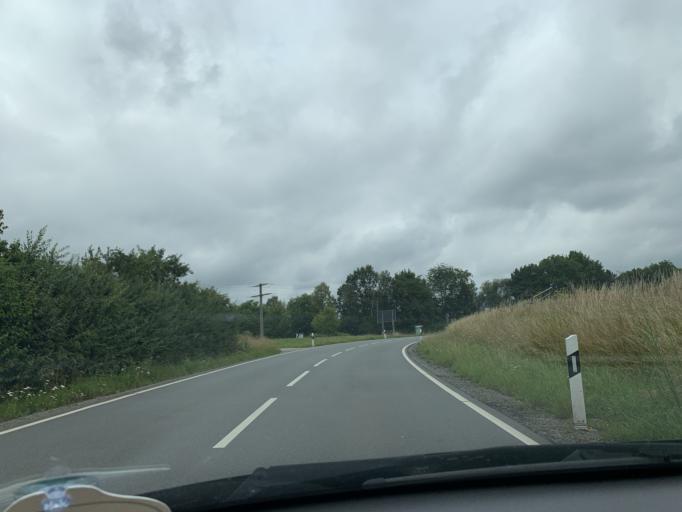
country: DE
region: North Rhine-Westphalia
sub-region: Regierungsbezirk Munster
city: Wadersloh
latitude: 51.7314
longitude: 8.2352
